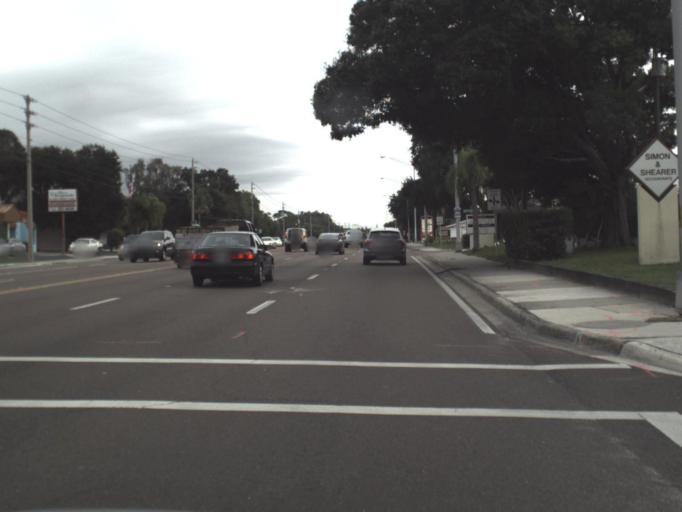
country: US
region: Florida
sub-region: Sarasota County
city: Ridge Wood Heights
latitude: 27.2988
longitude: -82.5224
